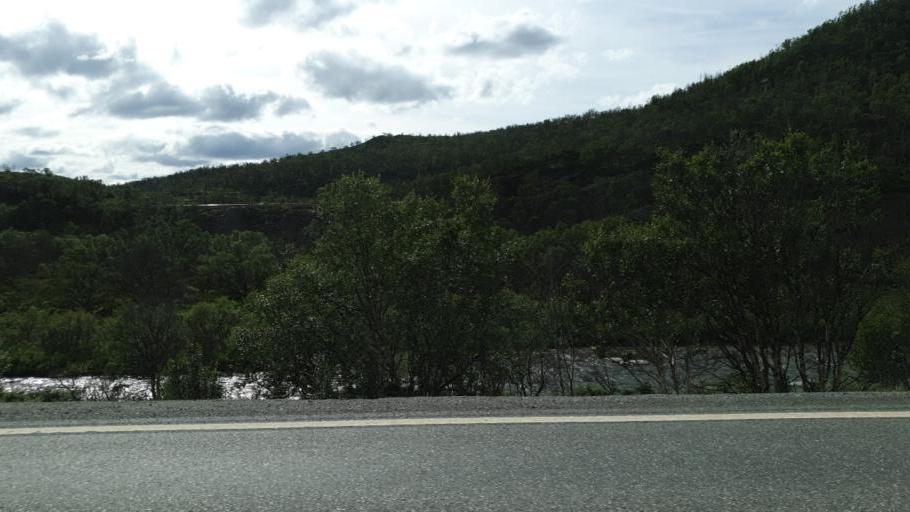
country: NO
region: Sor-Trondelag
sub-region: Oppdal
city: Oppdal
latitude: 62.2928
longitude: 9.5948
